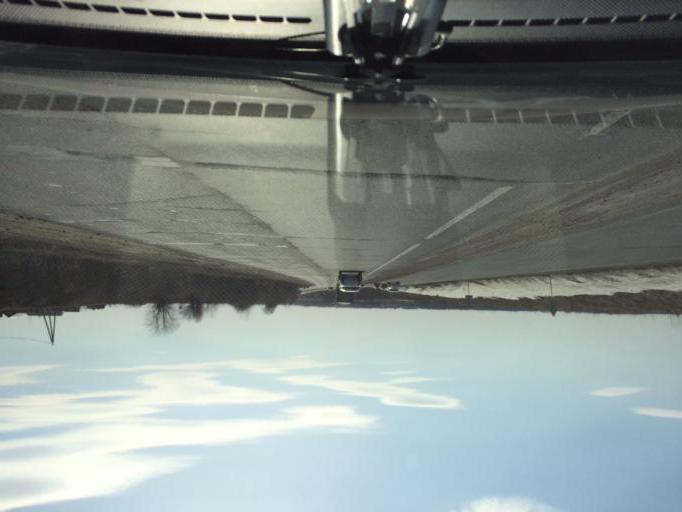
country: RU
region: Mariy-El
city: Yoshkar-Ola
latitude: 56.6913
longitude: 48.0517
